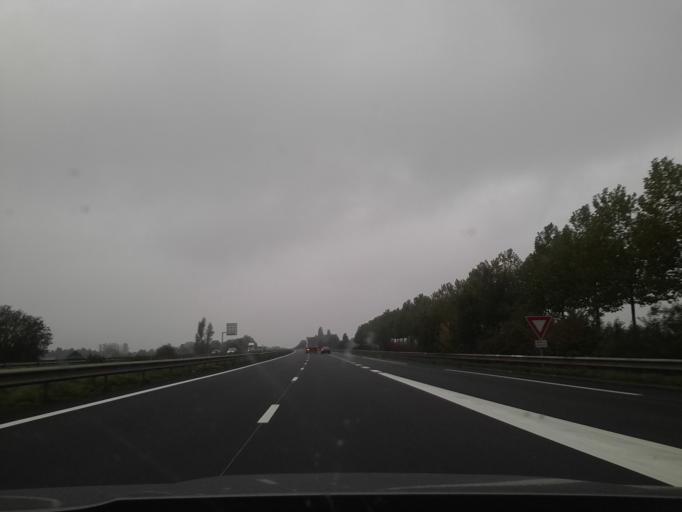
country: FR
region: Nord-Pas-de-Calais
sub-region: Departement du Nord
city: Vicq
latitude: 50.4026
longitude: 3.6180
